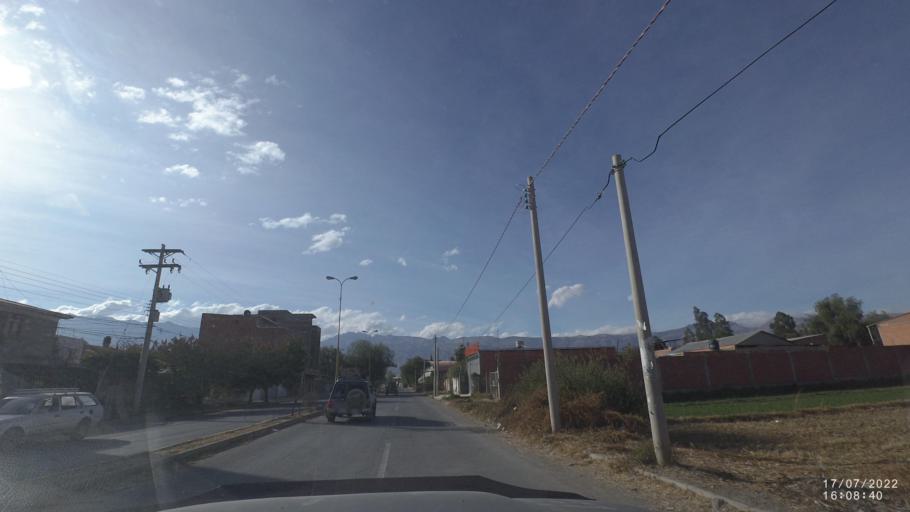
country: BO
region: Cochabamba
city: Cochabamba
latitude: -17.4068
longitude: -66.2734
